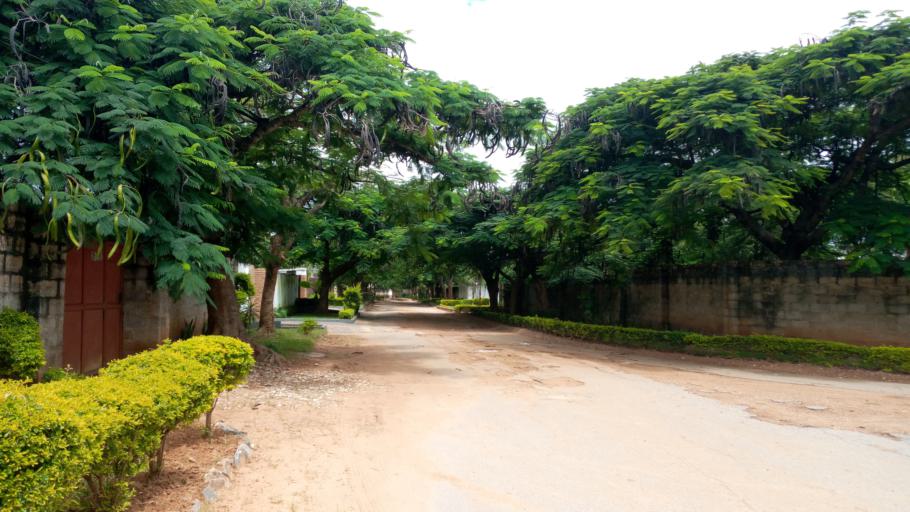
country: ZM
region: Lusaka
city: Lusaka
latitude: -15.4391
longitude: 28.3409
